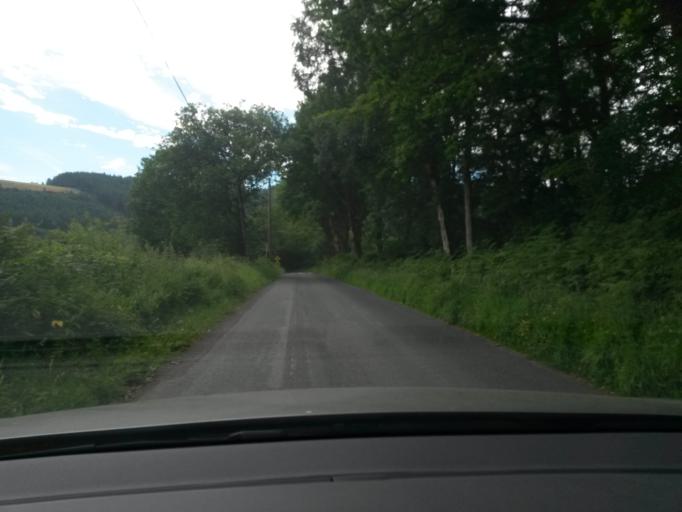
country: IE
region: Leinster
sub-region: Wicklow
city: Enniskerry
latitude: 53.1587
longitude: -6.2006
